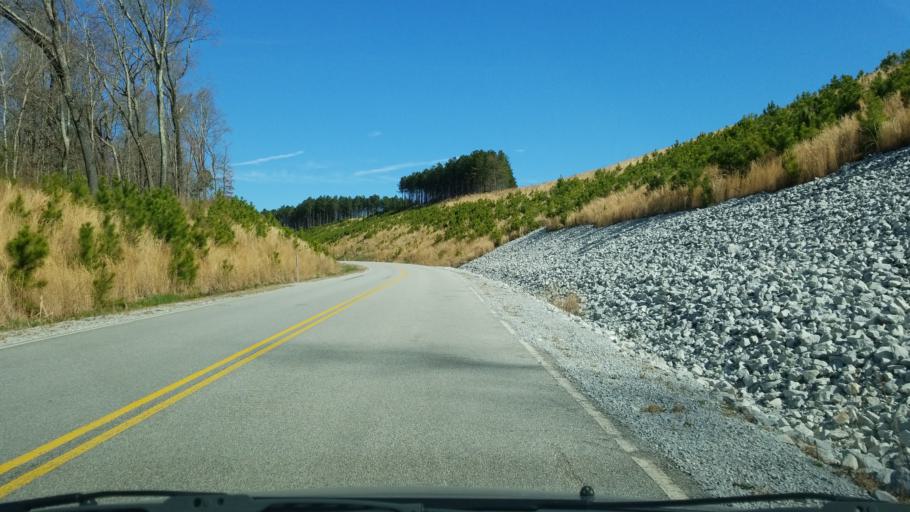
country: US
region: Tennessee
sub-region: Hamilton County
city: Harrison
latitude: 35.0997
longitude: -85.1366
